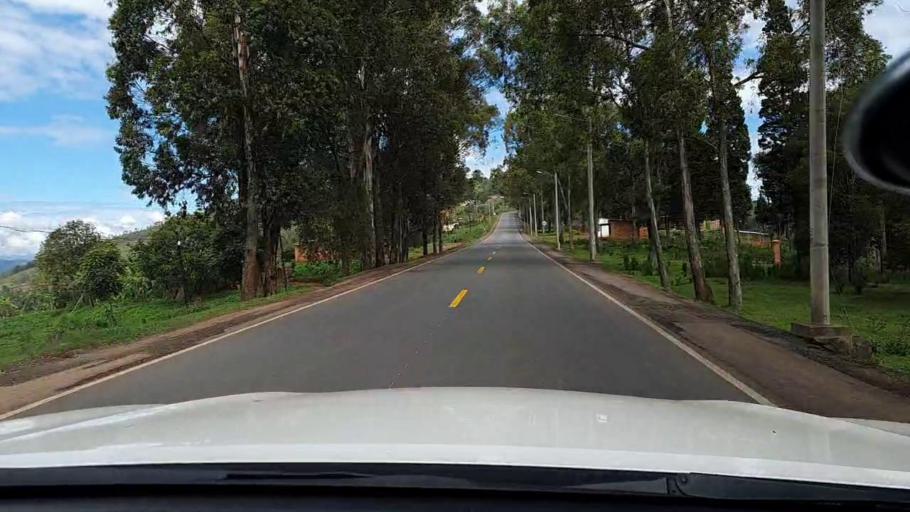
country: RW
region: Kigali
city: Kigali
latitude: -1.8338
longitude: 29.9514
